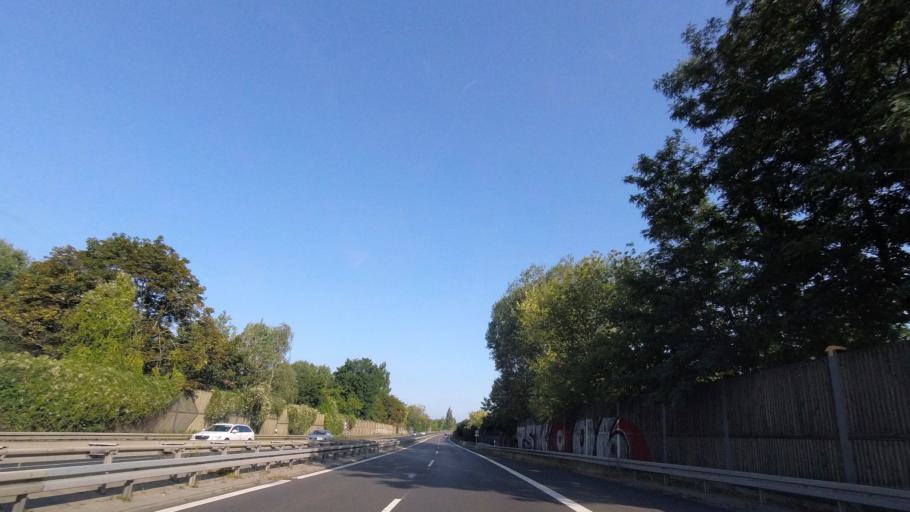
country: DE
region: Berlin
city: Bohnsdorf
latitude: 52.3945
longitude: 13.5640
